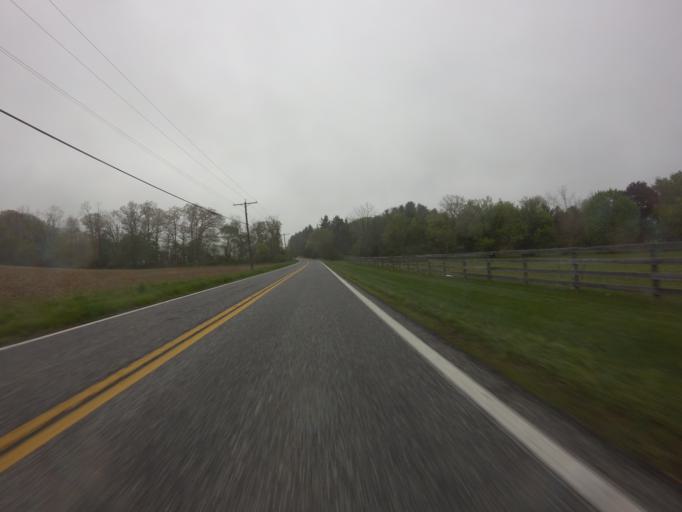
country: US
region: Maryland
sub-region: Baltimore County
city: Reisterstown
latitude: 39.4812
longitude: -76.7826
